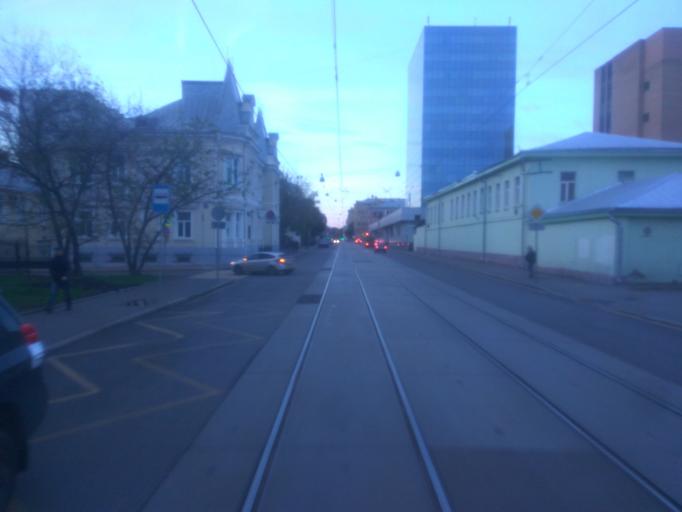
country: RU
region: Moscow
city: Lefortovo
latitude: 55.7667
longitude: 37.6799
